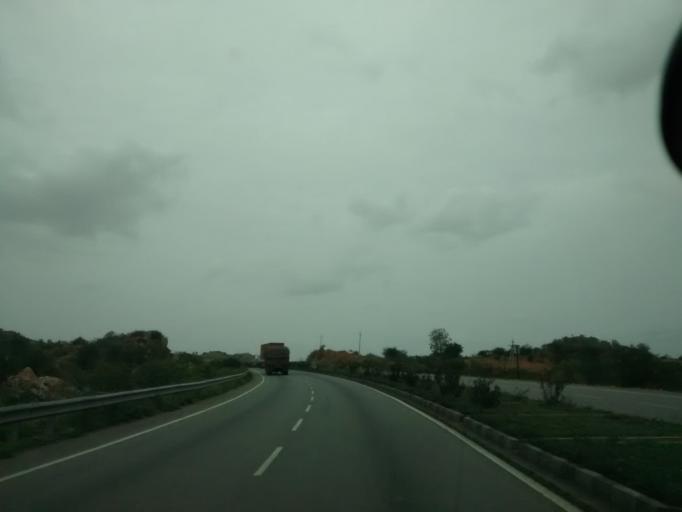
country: IN
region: Andhra Pradesh
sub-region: Kurnool
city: Ramapuram
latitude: 15.2003
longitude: 77.7122
